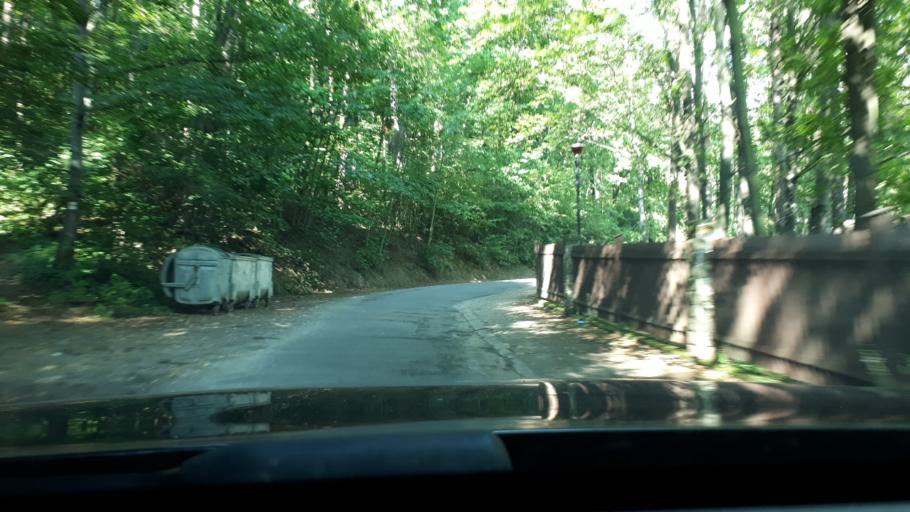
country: PL
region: Lower Silesian Voivodeship
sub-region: Powiat lubanski
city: Olszyna
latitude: 51.0190
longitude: 15.3308
